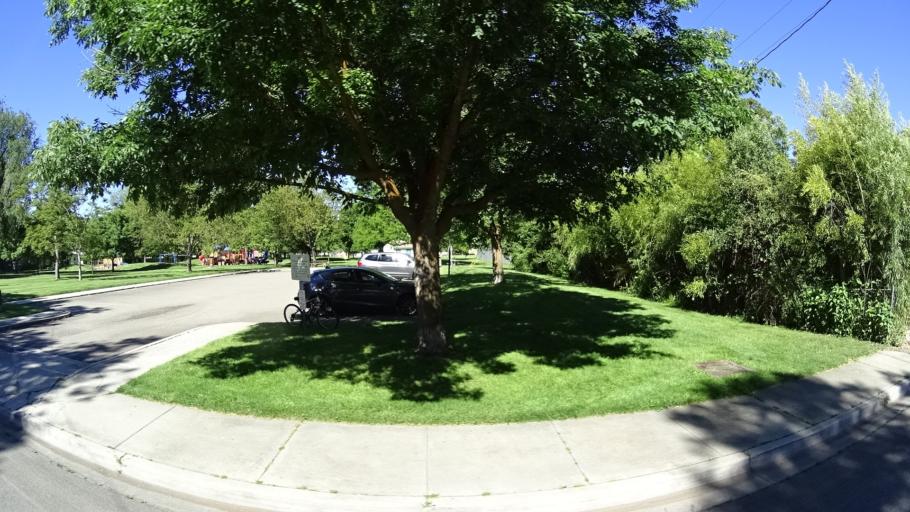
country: US
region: Idaho
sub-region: Ada County
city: Garden City
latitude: 43.6445
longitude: -116.2284
